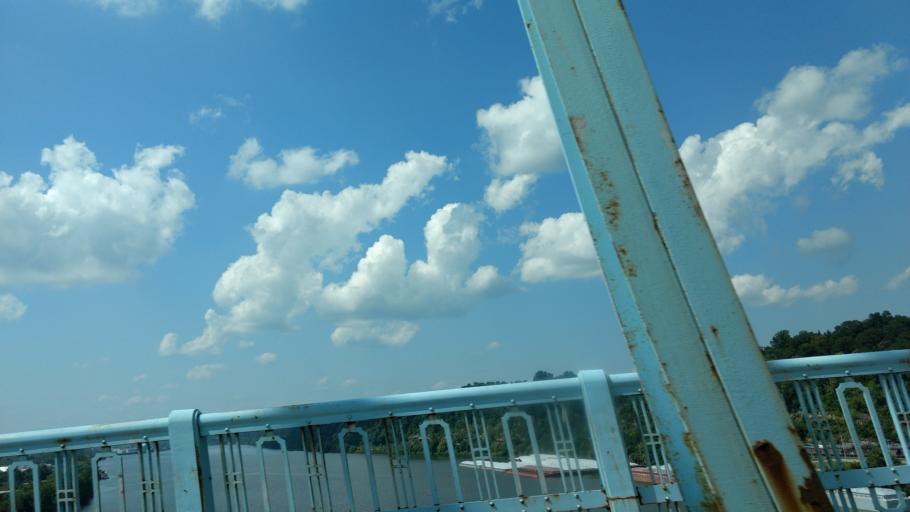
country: US
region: Pennsylvania
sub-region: Allegheny County
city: Bellevue
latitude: 40.4772
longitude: -80.0483
